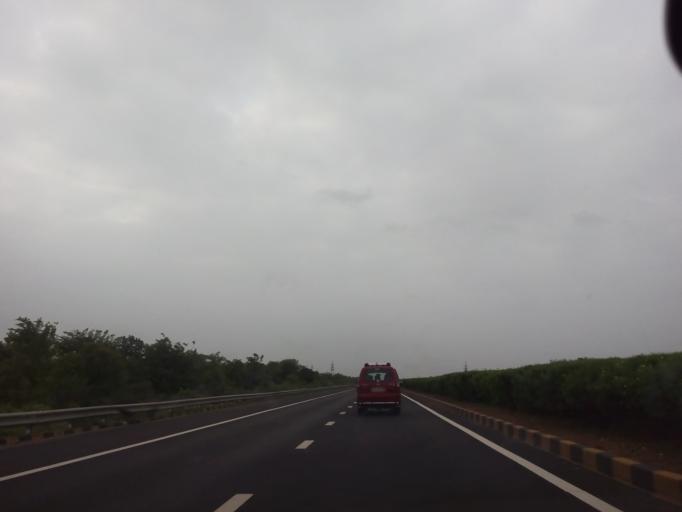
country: IN
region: Gujarat
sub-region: Kheda
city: Mahemdavad
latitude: 22.8012
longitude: 72.8384
